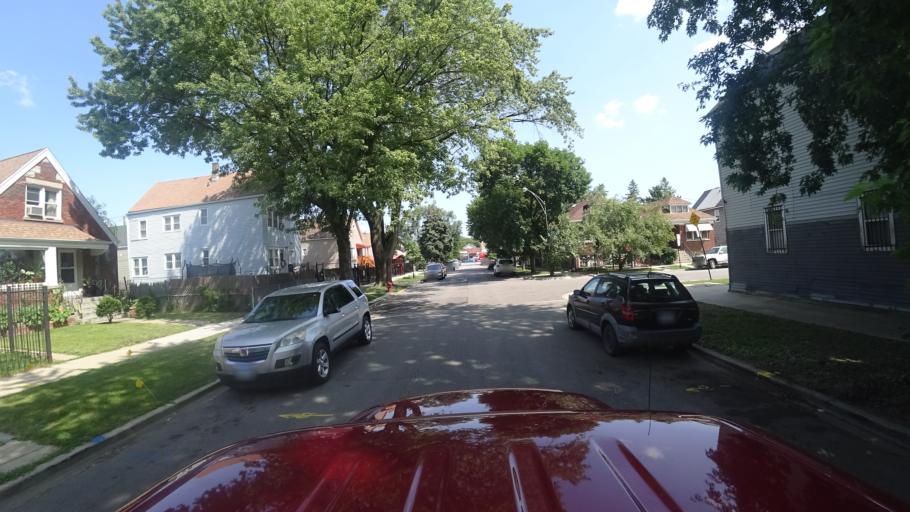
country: US
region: Illinois
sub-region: Cook County
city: Chicago
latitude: 41.8072
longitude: -87.6869
